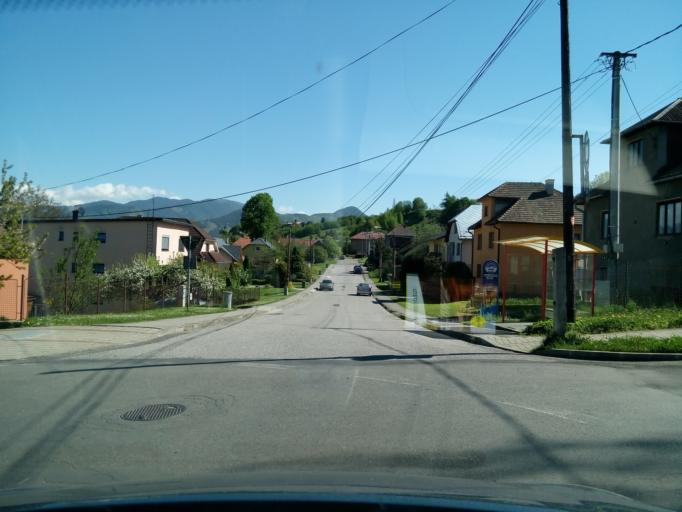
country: SK
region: Zilinsky
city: Ruzomberok
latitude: 49.0780
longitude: 19.2920
